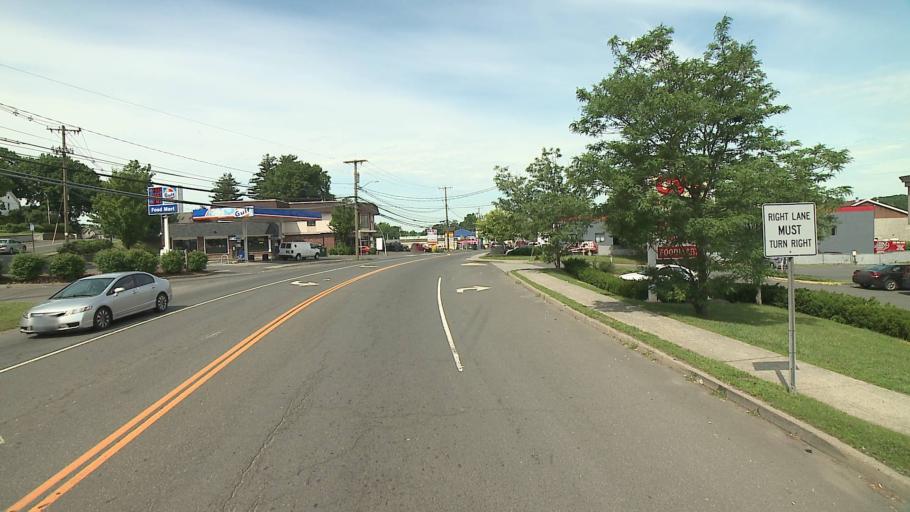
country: US
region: Connecticut
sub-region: Fairfield County
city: Danbury
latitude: 41.3994
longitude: -73.4310
